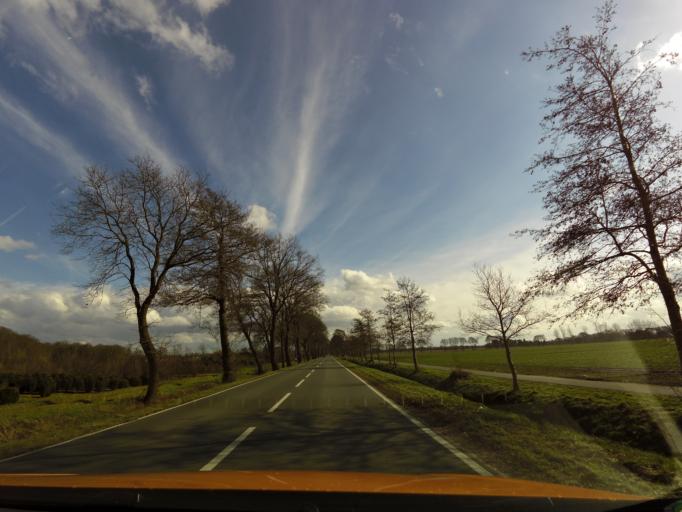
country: DE
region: Lower Saxony
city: Hatten
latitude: 53.0767
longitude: 8.2971
